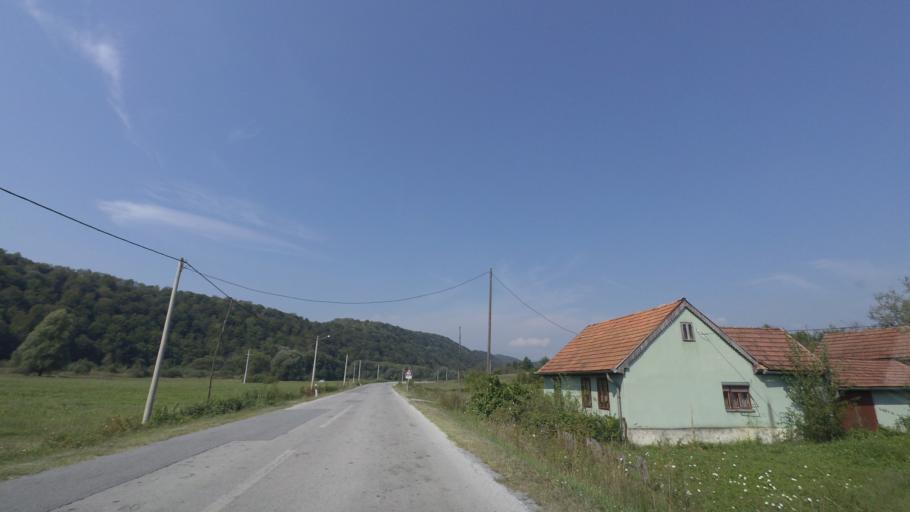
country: HR
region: Sisacko-Moslavacka
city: Dvor
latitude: 45.1155
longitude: 16.2716
